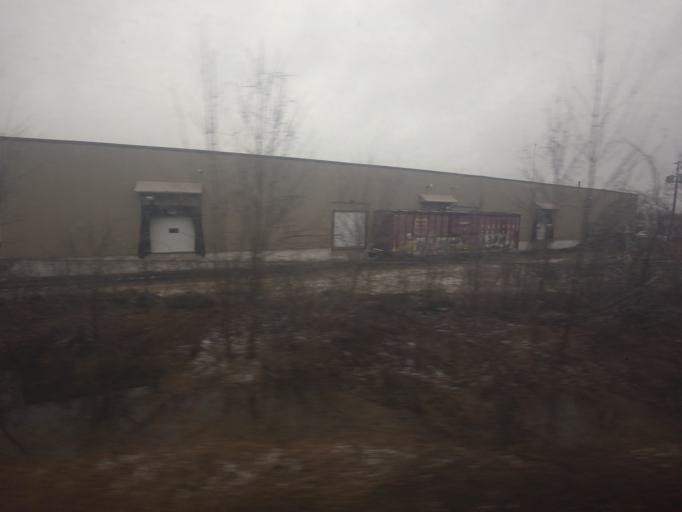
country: CA
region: Ontario
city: Brockville
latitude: 44.6090
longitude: -75.6947
